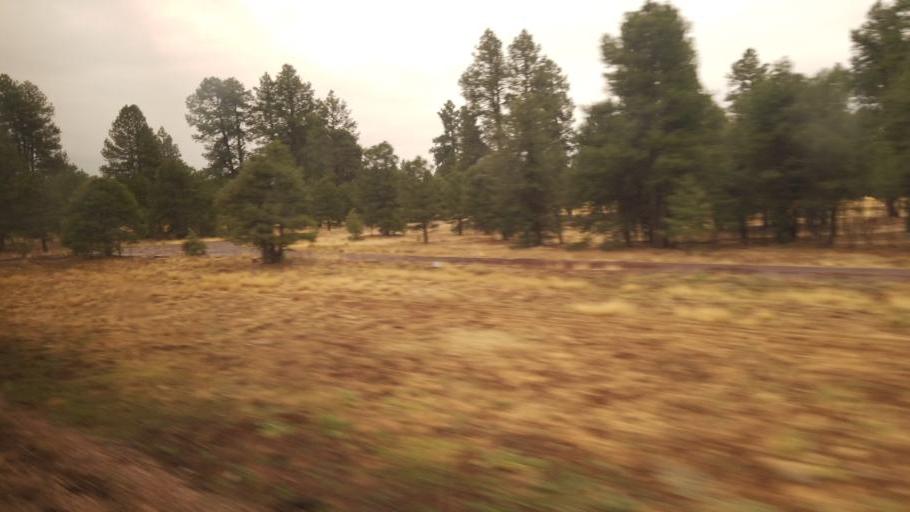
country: US
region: Arizona
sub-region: Coconino County
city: Parks
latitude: 35.2428
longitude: -111.8652
